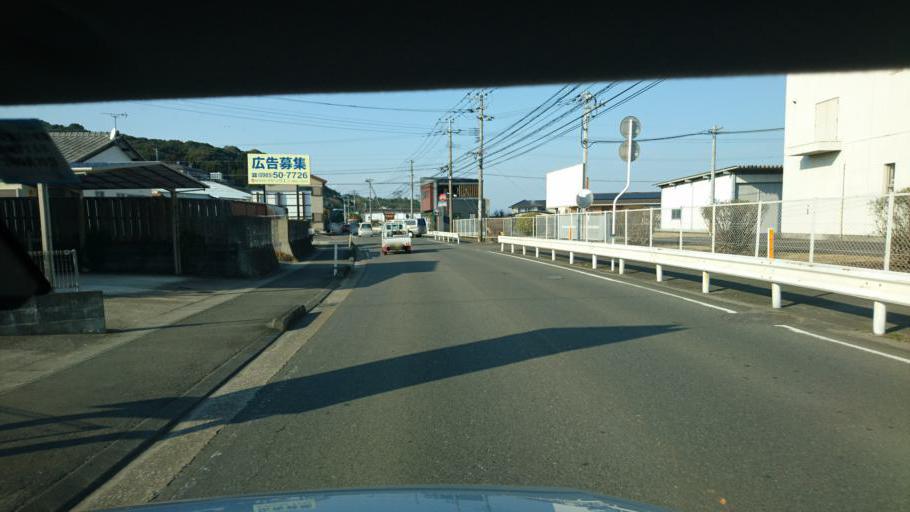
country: JP
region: Miyazaki
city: Miyazaki-shi
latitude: 31.9771
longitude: 131.4404
